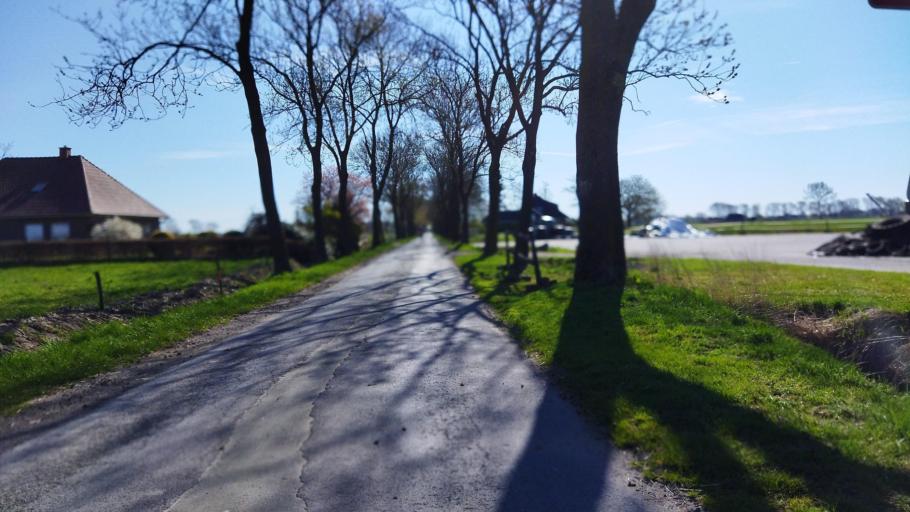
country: DE
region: Lower Saxony
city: Elsfleth
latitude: 53.2094
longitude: 8.4547
